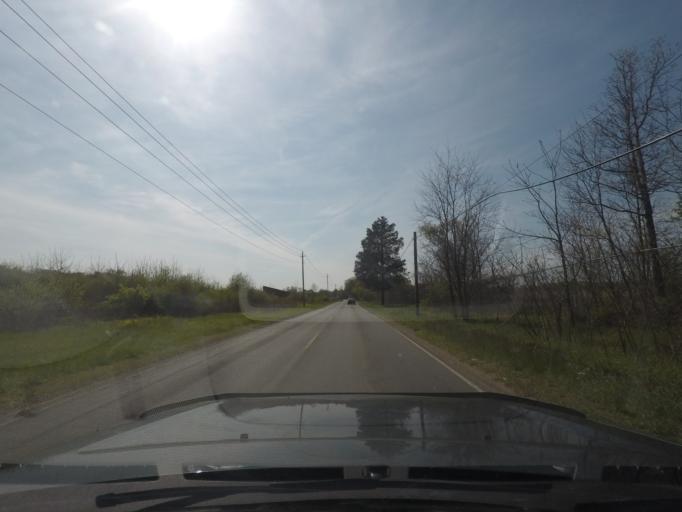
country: US
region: Indiana
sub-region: Elkhart County
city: Elkhart
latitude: 41.7040
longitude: -86.0057
